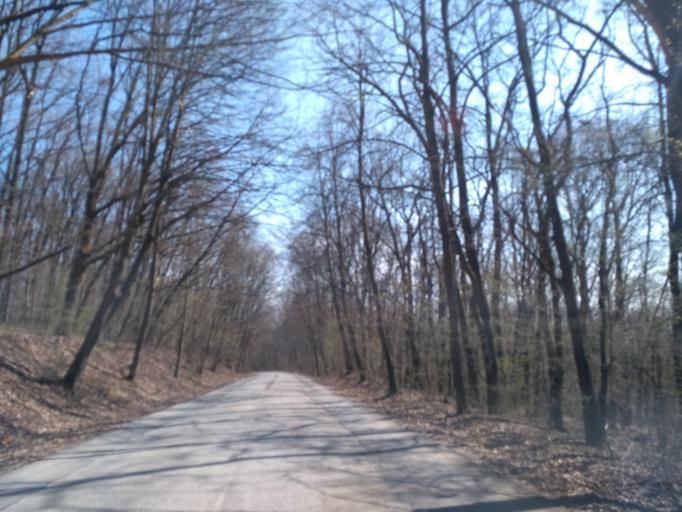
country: SK
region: Kosicky
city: Moldava nad Bodvou
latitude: 48.6481
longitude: 20.9967
